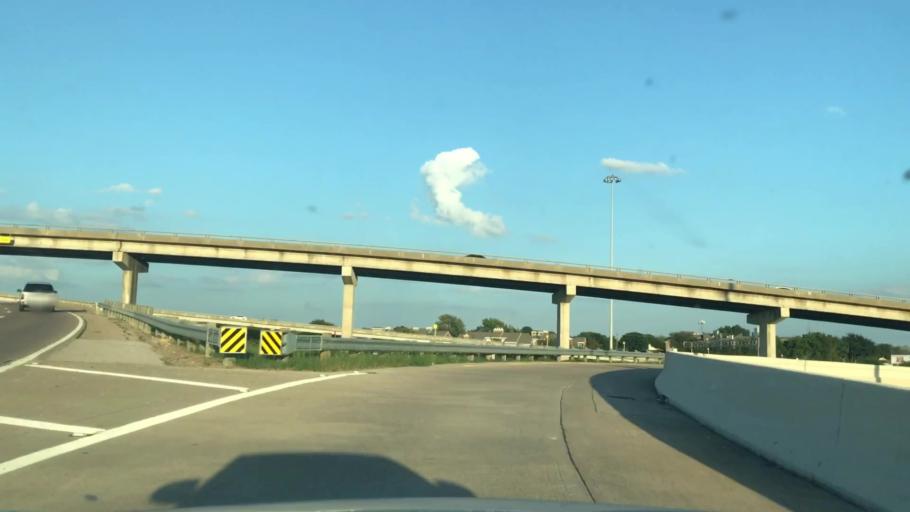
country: US
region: Texas
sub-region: Dallas County
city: Mesquite
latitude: 32.8212
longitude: -96.6308
